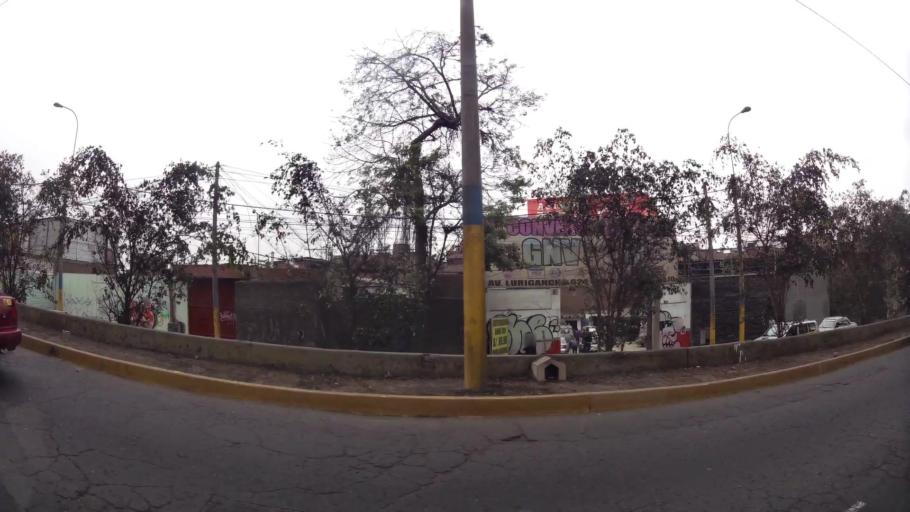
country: PE
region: Lima
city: Lima
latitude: -12.0195
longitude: -77.0039
